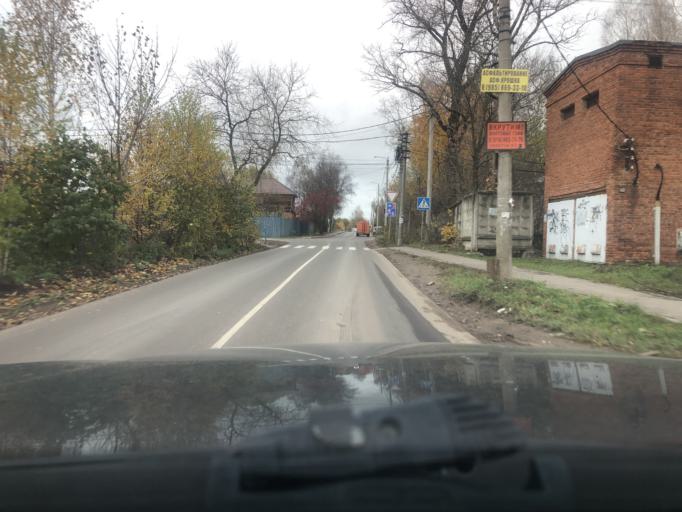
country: RU
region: Moskovskaya
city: Sergiyev Posad
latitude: 56.3057
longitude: 38.1093
